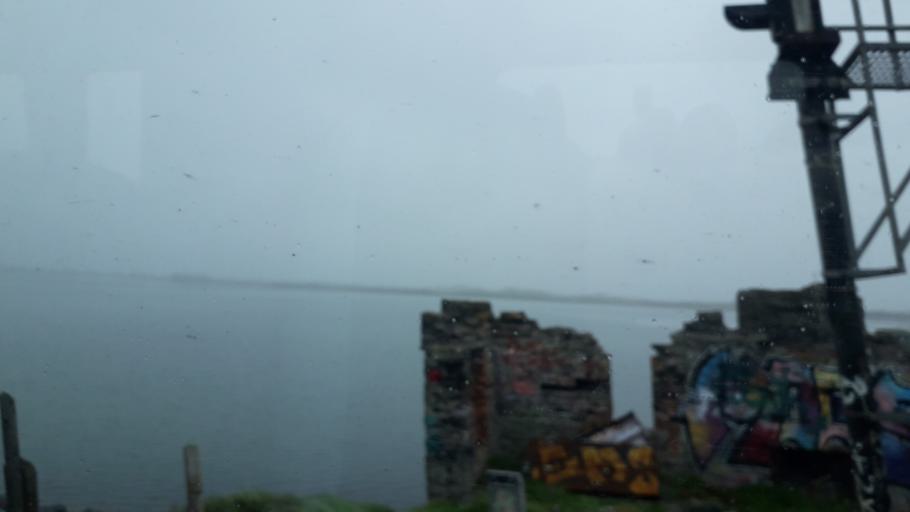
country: IE
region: Leinster
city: Malahide
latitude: 53.4594
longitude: -6.1553
